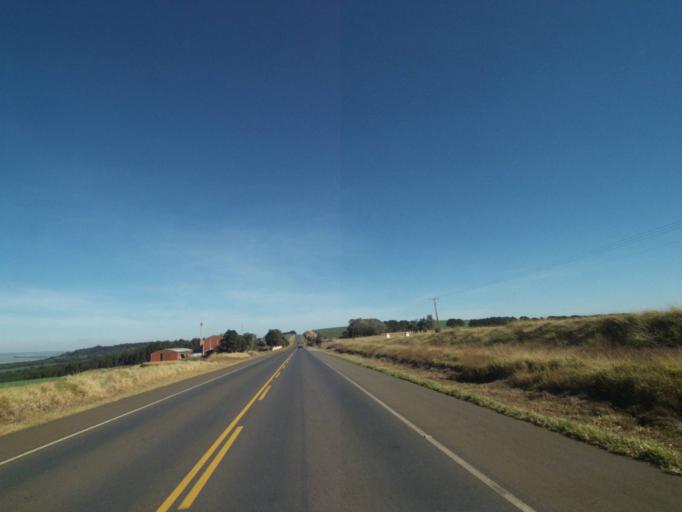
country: BR
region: Parana
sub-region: Tibagi
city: Tibagi
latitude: -24.3566
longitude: -50.3175
